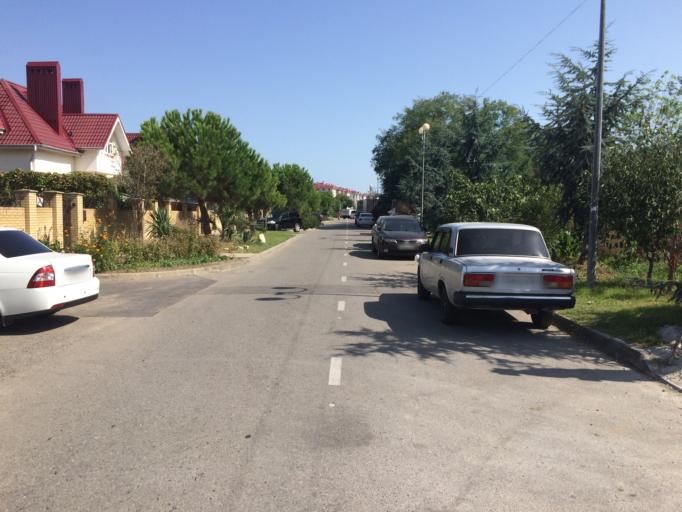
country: RU
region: Krasnodarskiy
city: Adler
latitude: 43.3981
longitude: 39.9701
